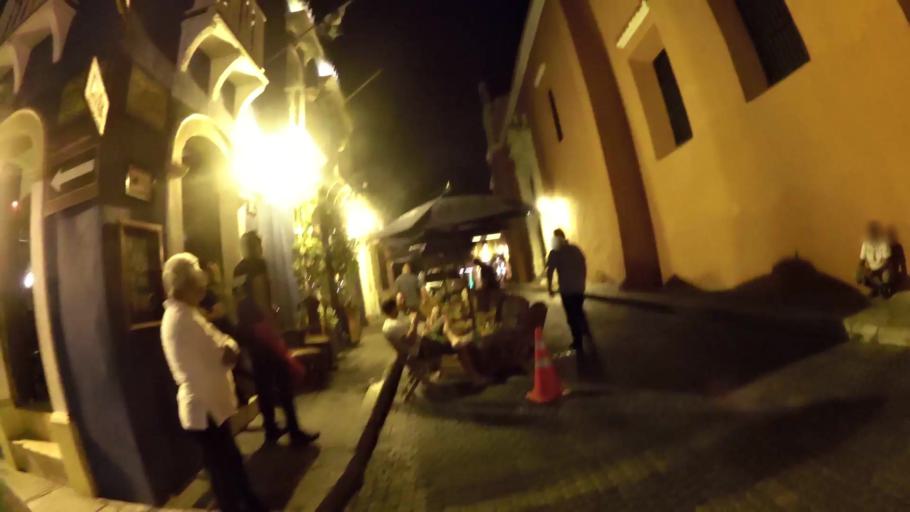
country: CO
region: Bolivar
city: Cartagena
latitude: 10.4280
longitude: -75.5473
